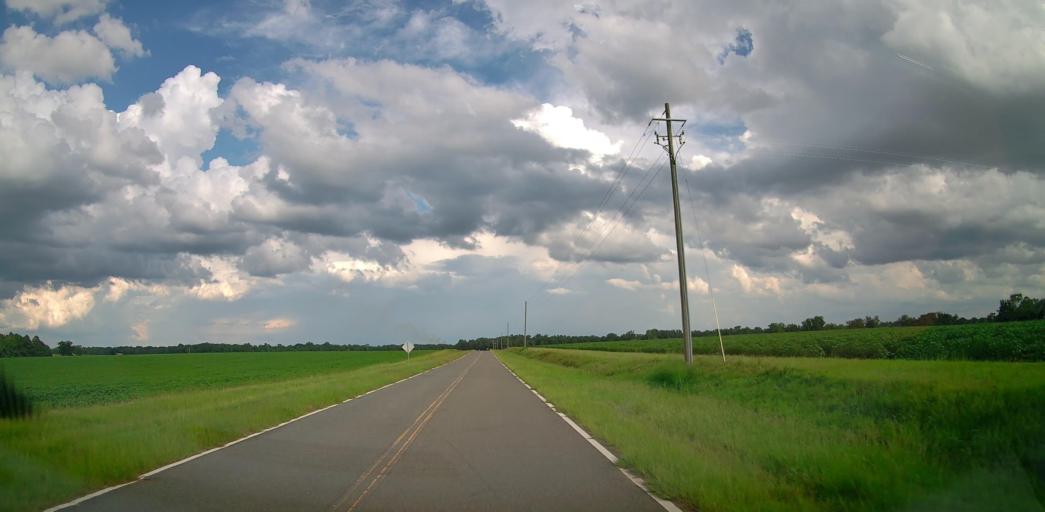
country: US
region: Georgia
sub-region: Bleckley County
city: Cochran
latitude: 32.4077
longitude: -83.4263
